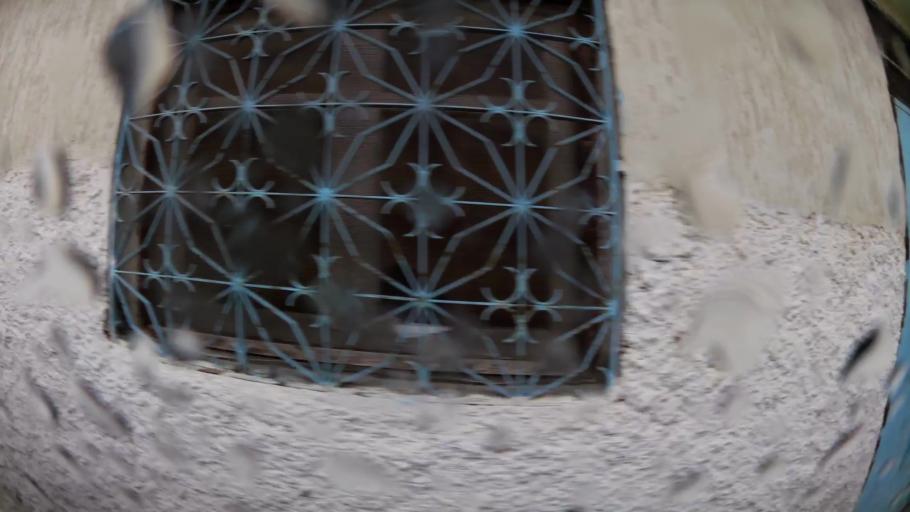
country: MA
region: Tanger-Tetouan
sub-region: Tetouan
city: Martil
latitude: 35.6192
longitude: -5.2805
